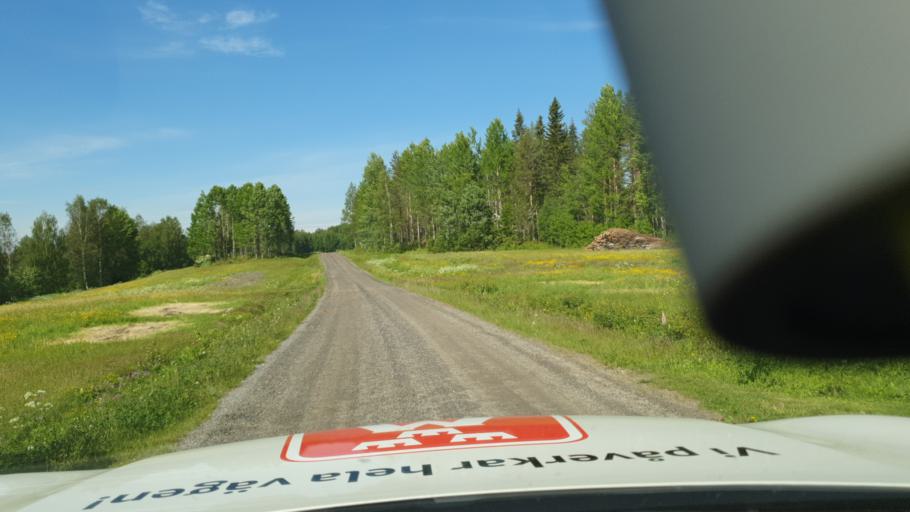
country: SE
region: Vaesterbotten
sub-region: Robertsfors Kommun
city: Robertsfors
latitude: 64.2013
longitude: 20.7027
